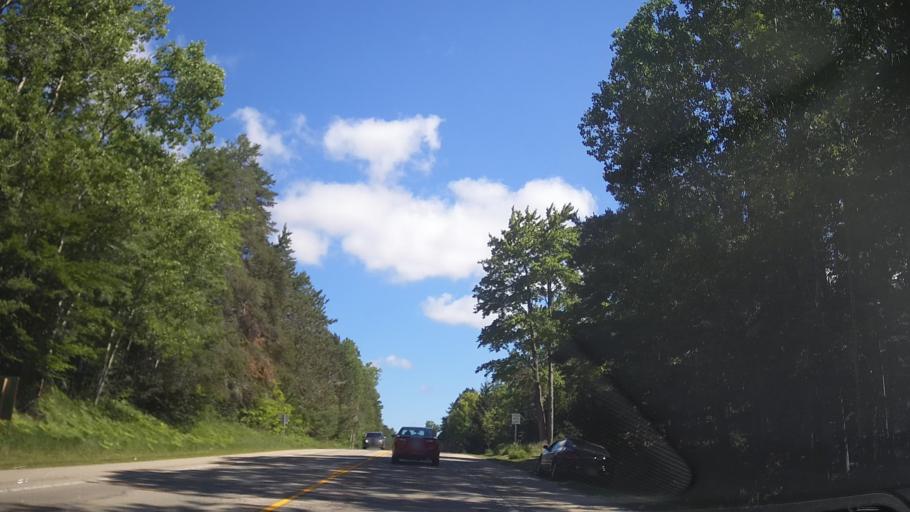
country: US
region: Michigan
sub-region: Cheboygan County
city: Indian River
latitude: 45.4576
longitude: -84.7833
